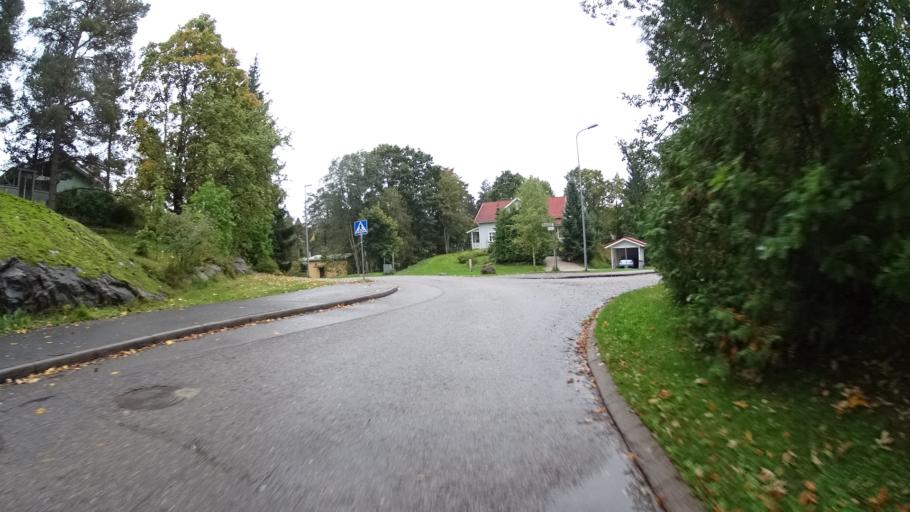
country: FI
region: Uusimaa
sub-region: Helsinki
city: Kauniainen
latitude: 60.3221
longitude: 24.7158
